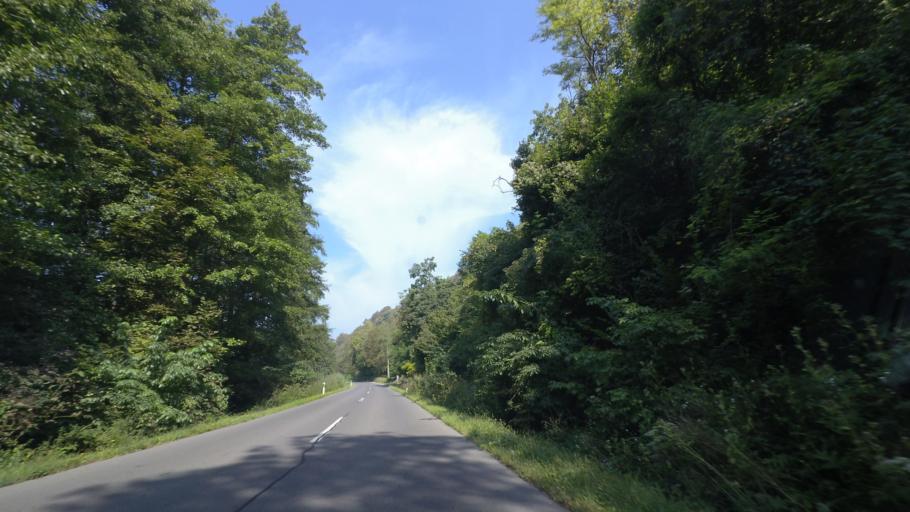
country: BA
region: Republika Srpska
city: Kostajnica
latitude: 45.2197
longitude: 16.6290
